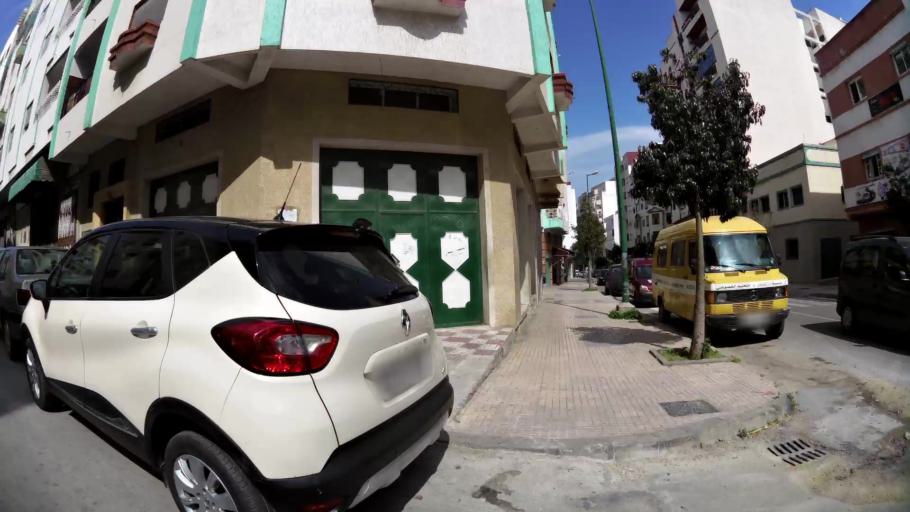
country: MA
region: Tanger-Tetouan
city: Tetouan
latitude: 35.5841
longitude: -5.3518
